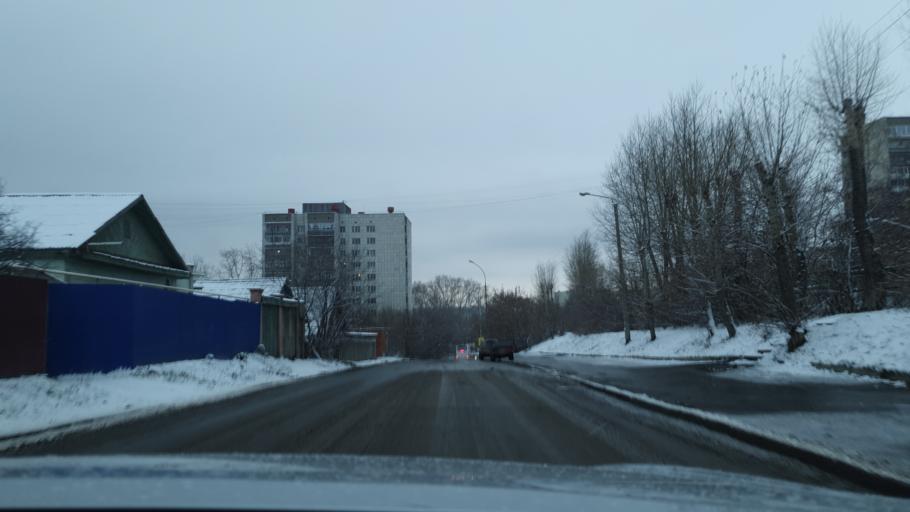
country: RU
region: Sverdlovsk
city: Istok
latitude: 56.7495
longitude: 60.7066
